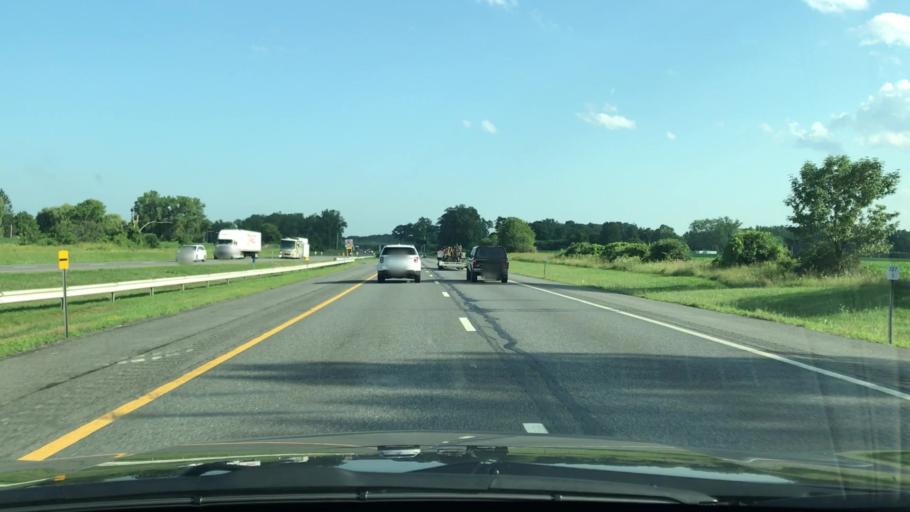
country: US
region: New York
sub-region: Rensselaer County
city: Castleton-on-Hudson
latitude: 42.5645
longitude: -73.7892
